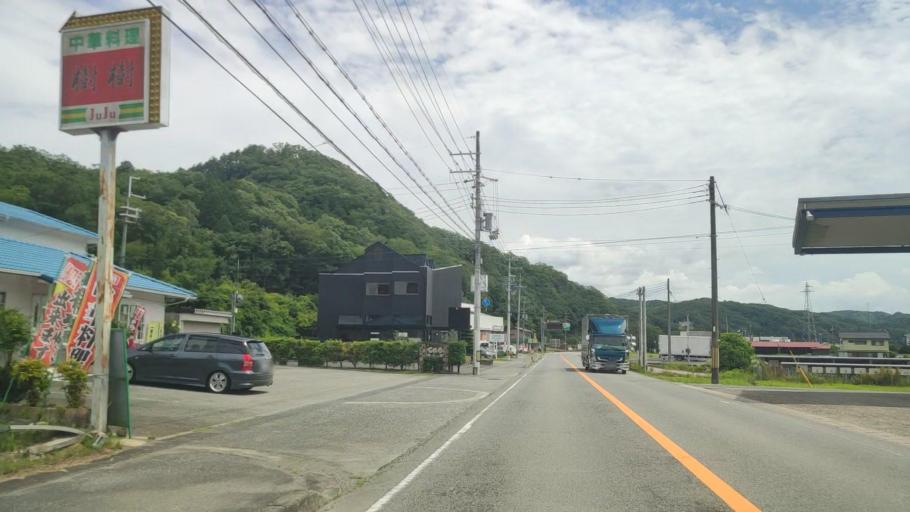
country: JP
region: Hyogo
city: Yamazakicho-nakabirose
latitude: 35.0276
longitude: 134.3702
